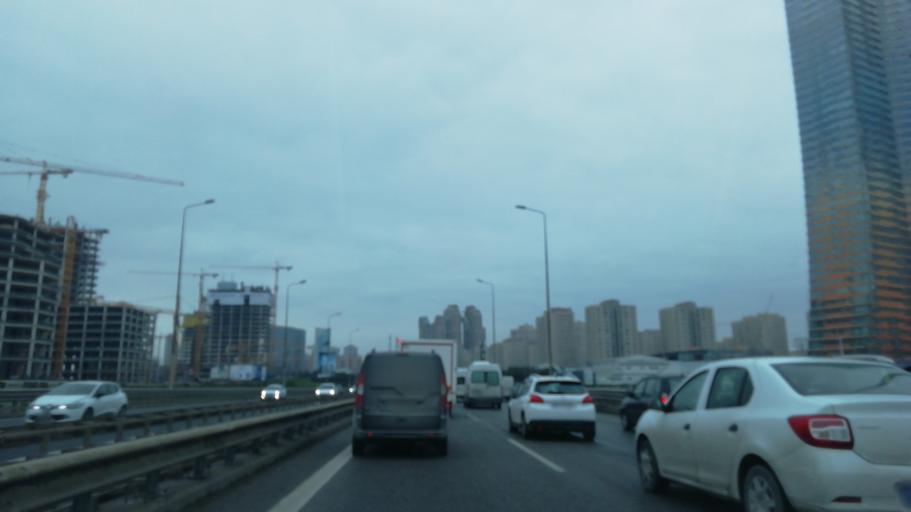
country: TR
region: Istanbul
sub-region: Atasehir
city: Atasehir
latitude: 41.0033
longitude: 29.1027
